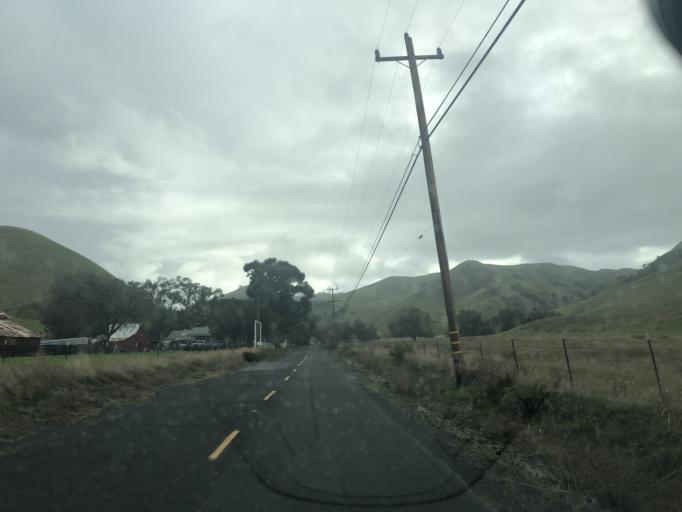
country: US
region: California
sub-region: Contra Costa County
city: Pittsburg
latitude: 37.9800
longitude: -121.8976
